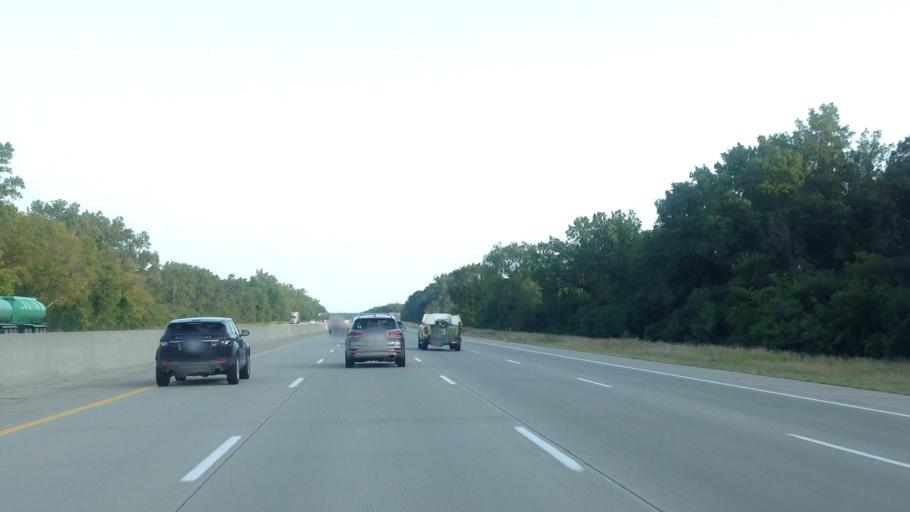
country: US
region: Michigan
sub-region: Saginaw County
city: Bridgeport
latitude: 43.3135
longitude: -83.8415
